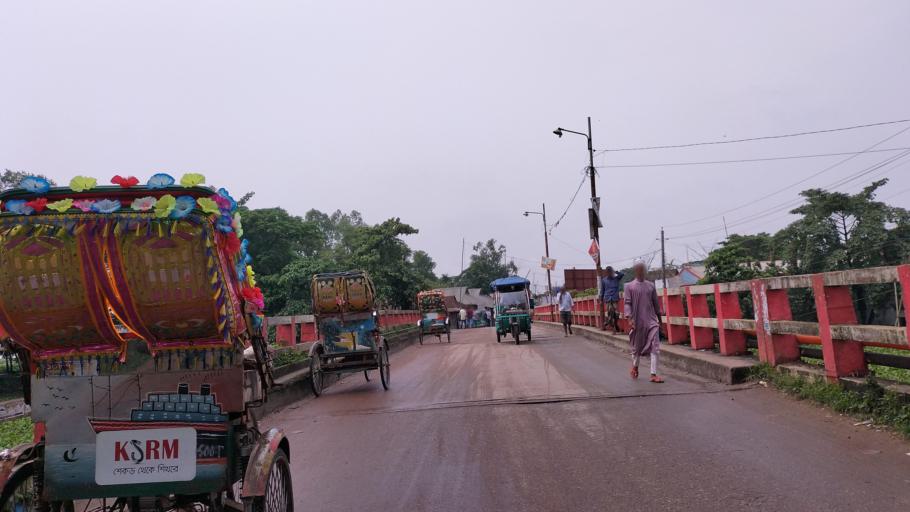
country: BD
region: Dhaka
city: Netrakona
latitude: 24.8925
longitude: 90.7389
